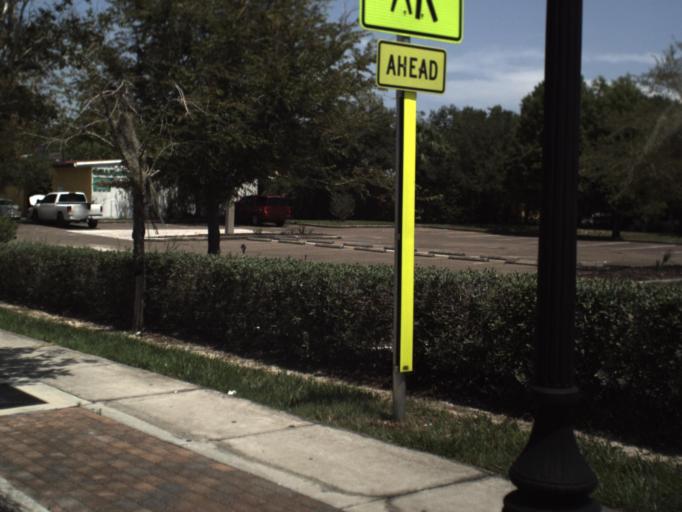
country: US
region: Florida
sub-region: Pinellas County
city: Tarpon Springs
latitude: 28.1497
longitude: -82.7567
